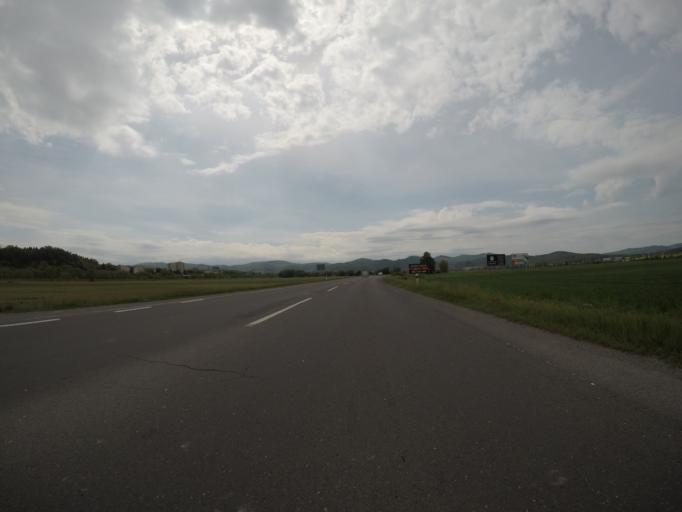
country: SK
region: Banskobystricky
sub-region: Okres Banska Bystrica
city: Zvolen
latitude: 48.6006
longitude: 19.1249
